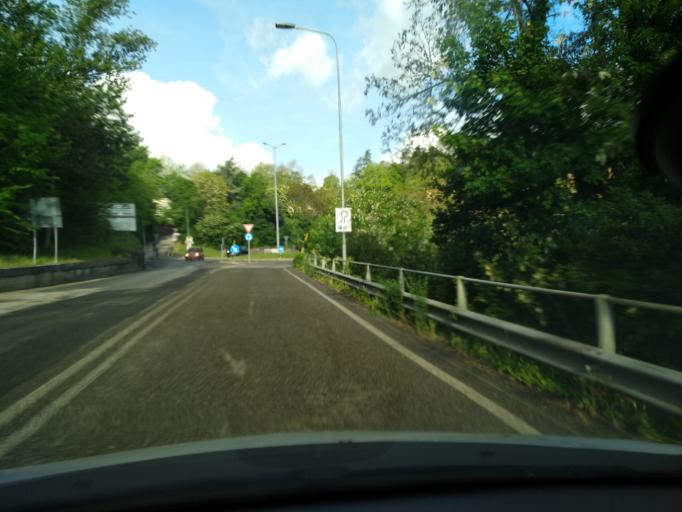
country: IT
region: The Marches
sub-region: Provincia di Pesaro e Urbino
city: Urbino
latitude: 43.7302
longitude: 12.6340
